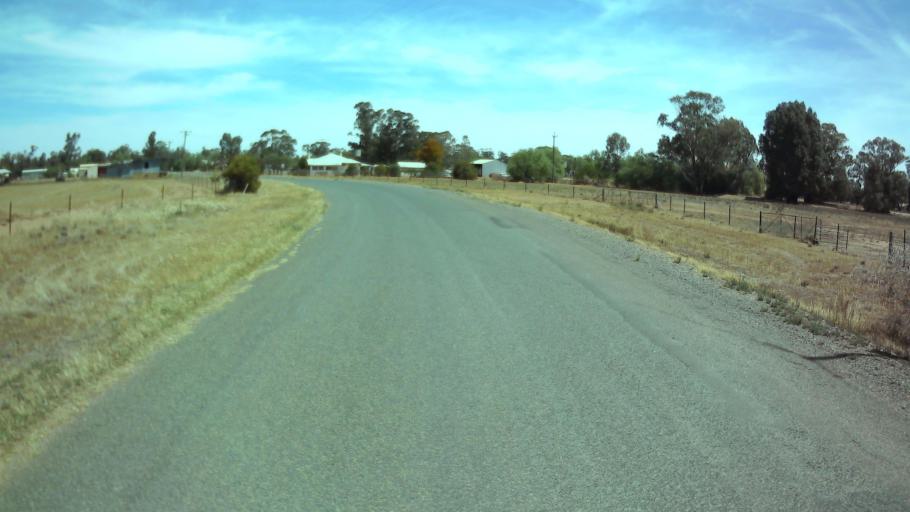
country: AU
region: New South Wales
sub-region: Weddin
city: Grenfell
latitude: -33.8387
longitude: 147.7450
